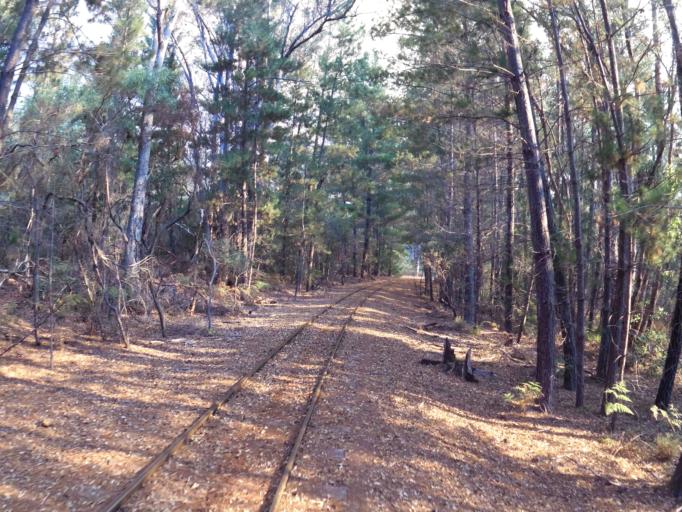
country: AU
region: Western Australia
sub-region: Waroona
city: Waroona
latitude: -32.7379
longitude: 116.1308
